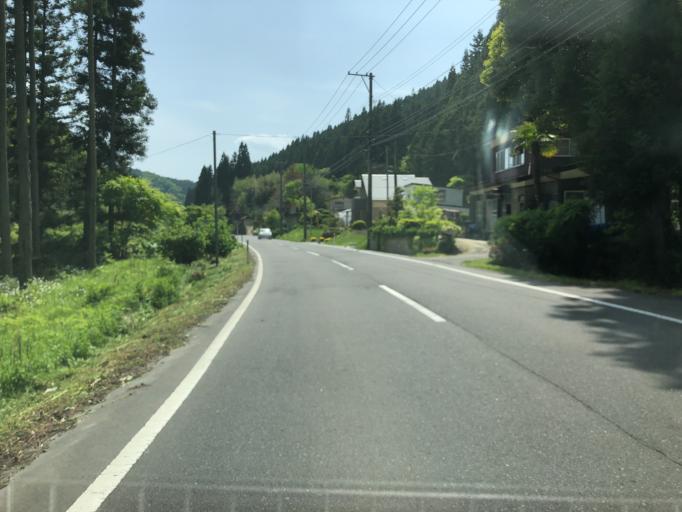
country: JP
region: Fukushima
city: Ishikawa
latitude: 37.1526
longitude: 140.4806
